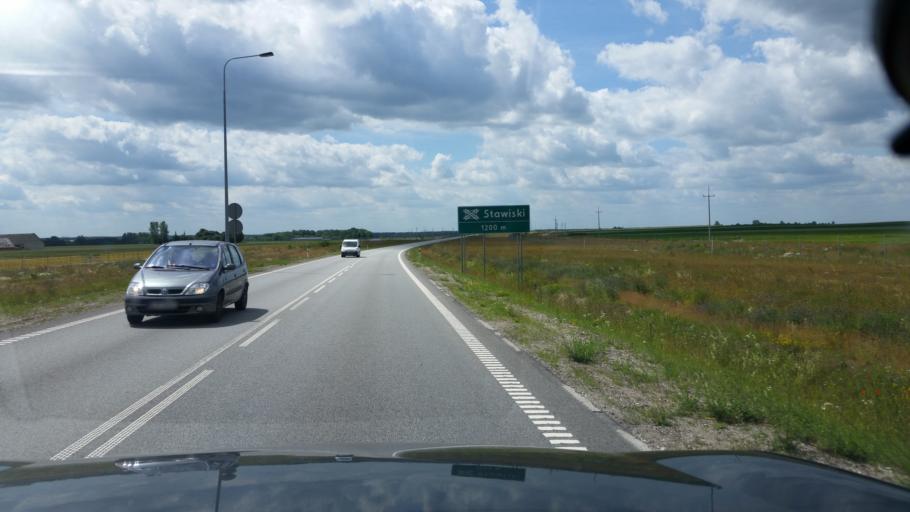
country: PL
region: Podlasie
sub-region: Powiat kolnenski
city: Stawiski
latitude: 53.4004
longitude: 22.1567
